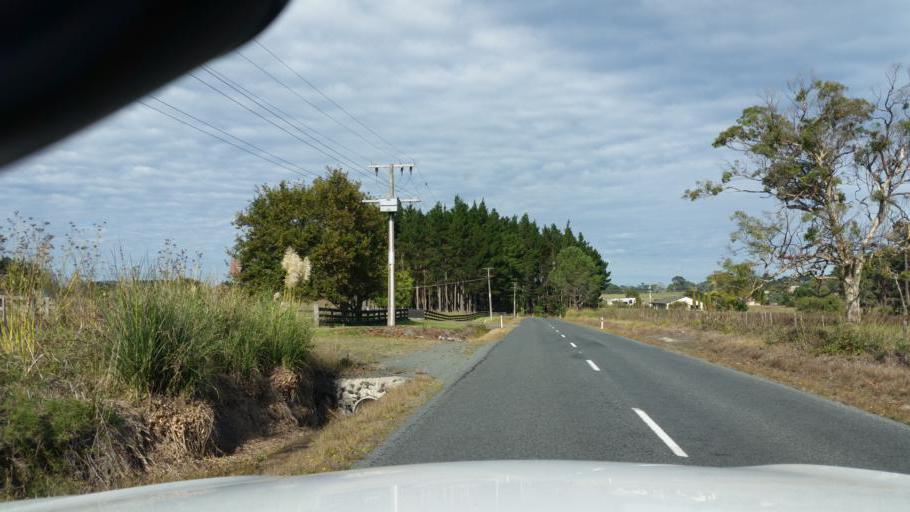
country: NZ
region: Northland
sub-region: Kaipara District
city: Dargaville
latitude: -35.9169
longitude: 173.8228
